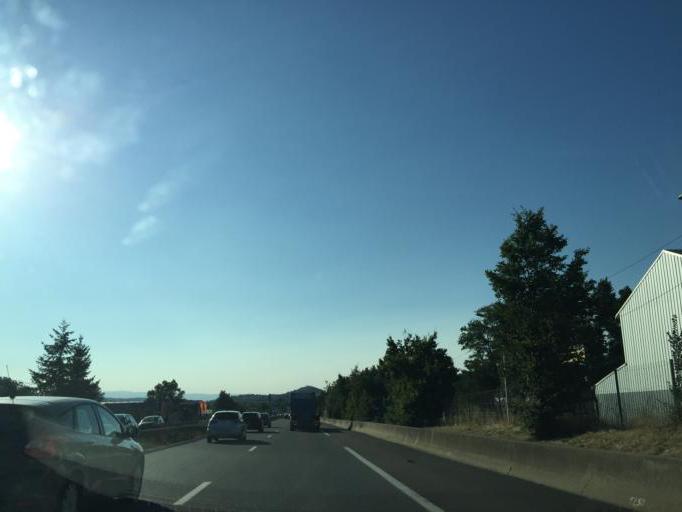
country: FR
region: Rhone-Alpes
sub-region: Departement de la Loire
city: La Talaudiere
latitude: 45.4516
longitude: 4.4183
